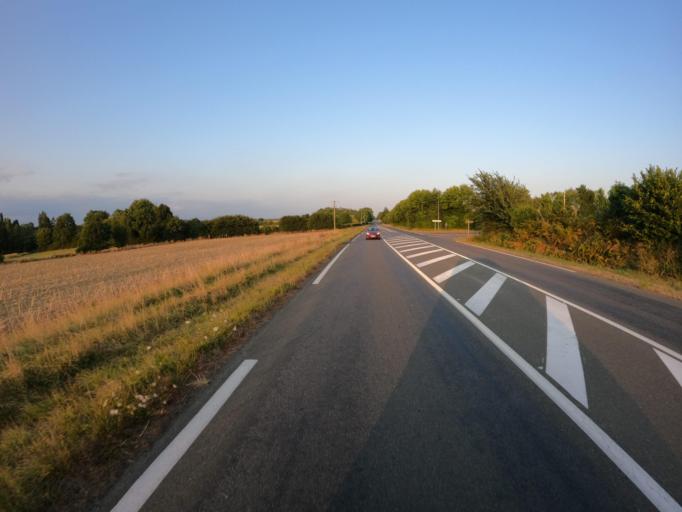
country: FR
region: Pays de la Loire
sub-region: Departement de la Mayenne
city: Meslay-du-Maine
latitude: 47.8728
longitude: -0.5055
